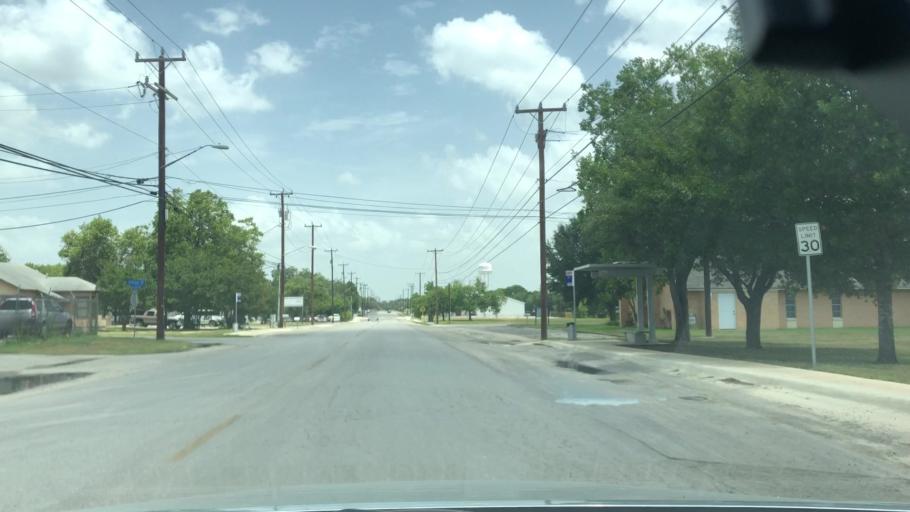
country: US
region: Texas
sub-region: Bexar County
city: Kirby
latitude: 29.4664
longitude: -98.3914
